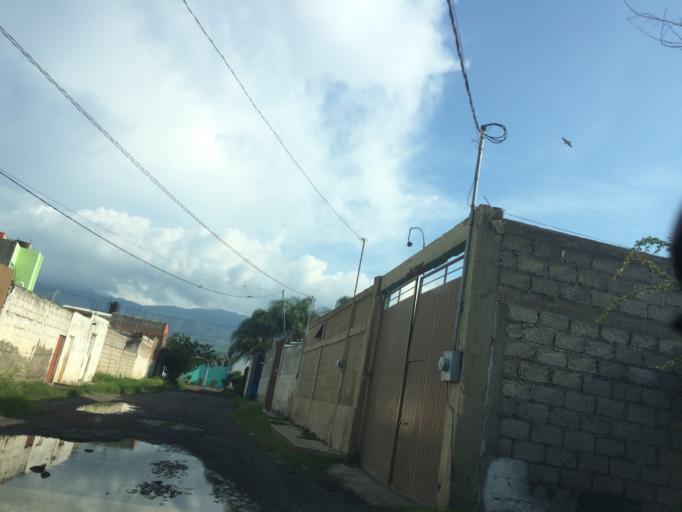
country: MX
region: Nayarit
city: Ixtlan del Rio
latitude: 21.0348
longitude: -104.3886
